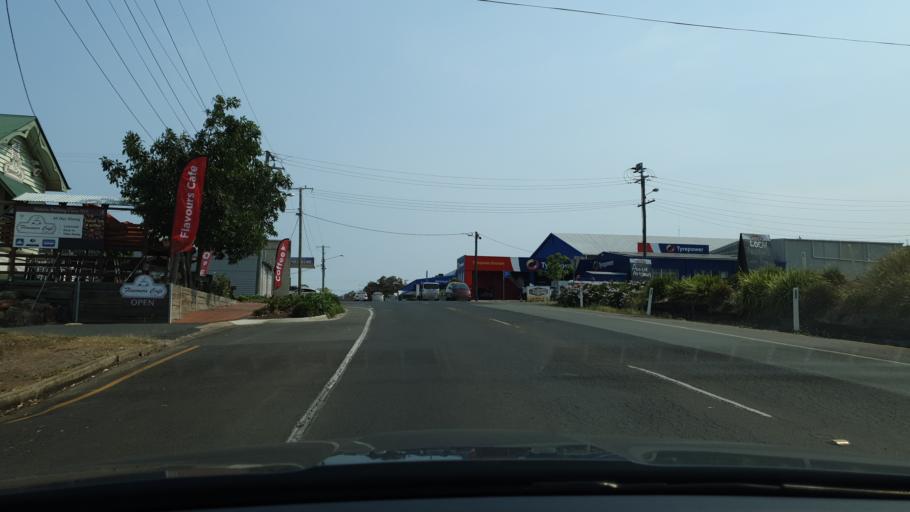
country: AU
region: Queensland
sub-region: Ipswich
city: Deebing Heights
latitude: -27.9953
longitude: 152.6819
